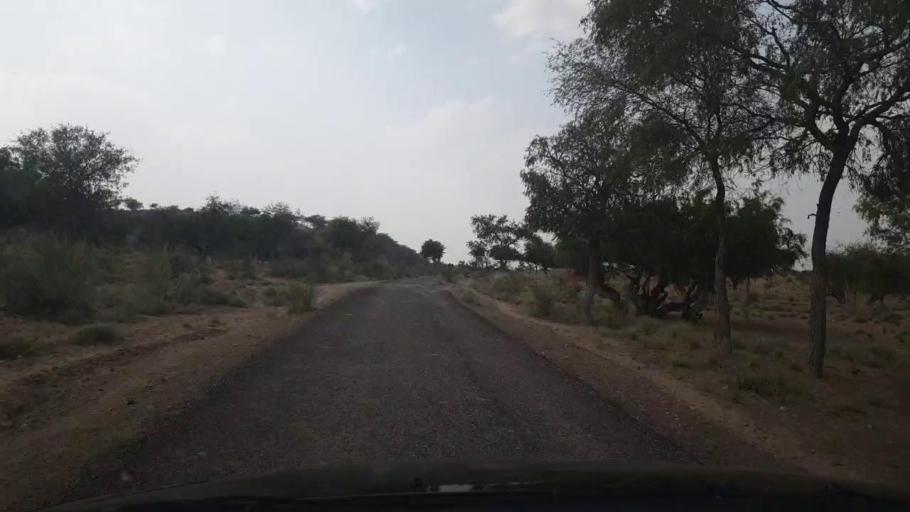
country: PK
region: Sindh
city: Islamkot
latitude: 24.9657
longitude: 70.6043
